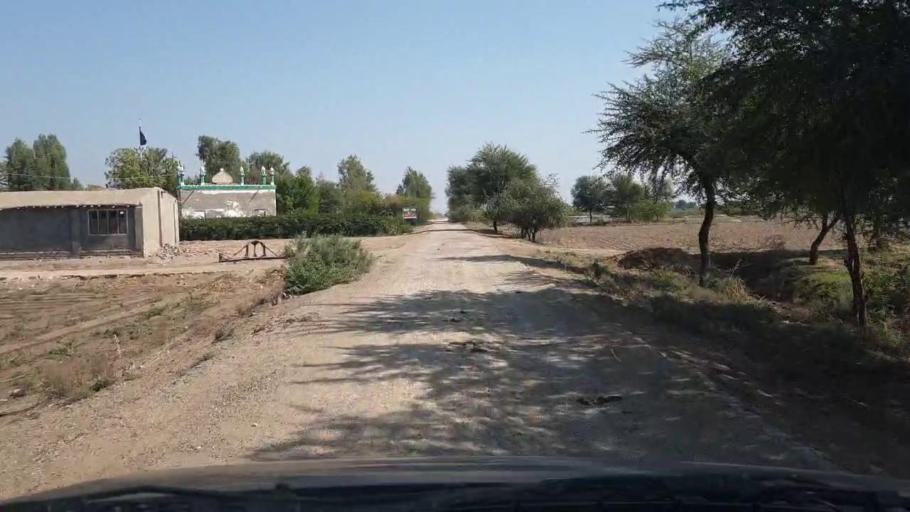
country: PK
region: Sindh
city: Samaro
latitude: 25.2025
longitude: 69.2835
